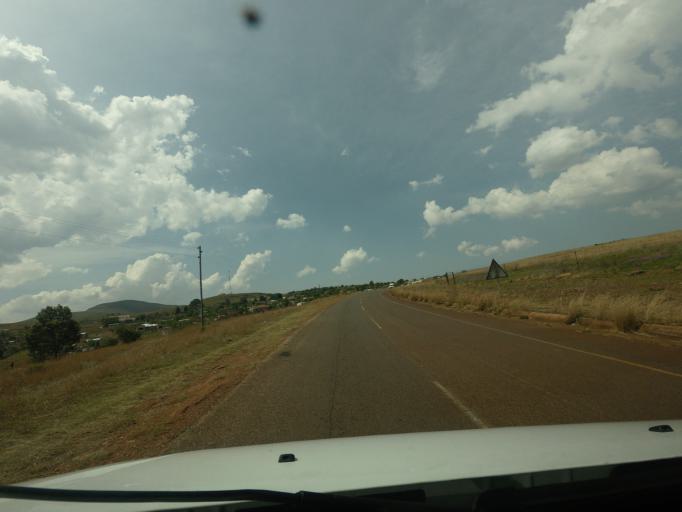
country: ZA
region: Mpumalanga
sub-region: Ehlanzeni District
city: Graksop
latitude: -24.6666
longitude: 30.8099
